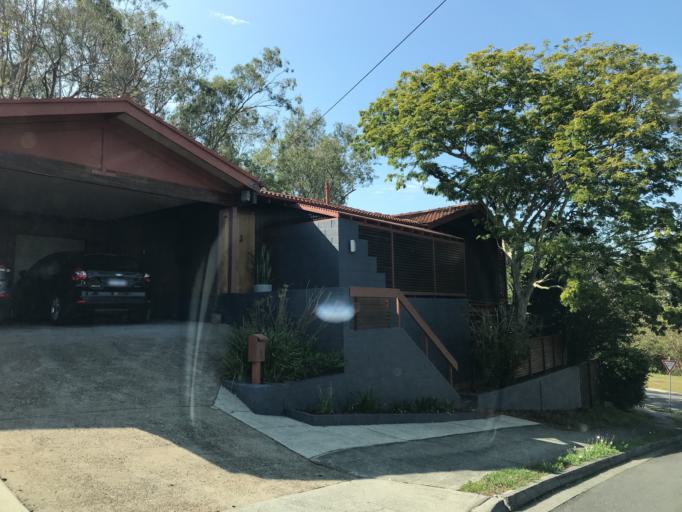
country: AU
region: Queensland
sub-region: Moreton Bay
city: Ferny Hills
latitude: -27.4416
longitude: 152.9396
